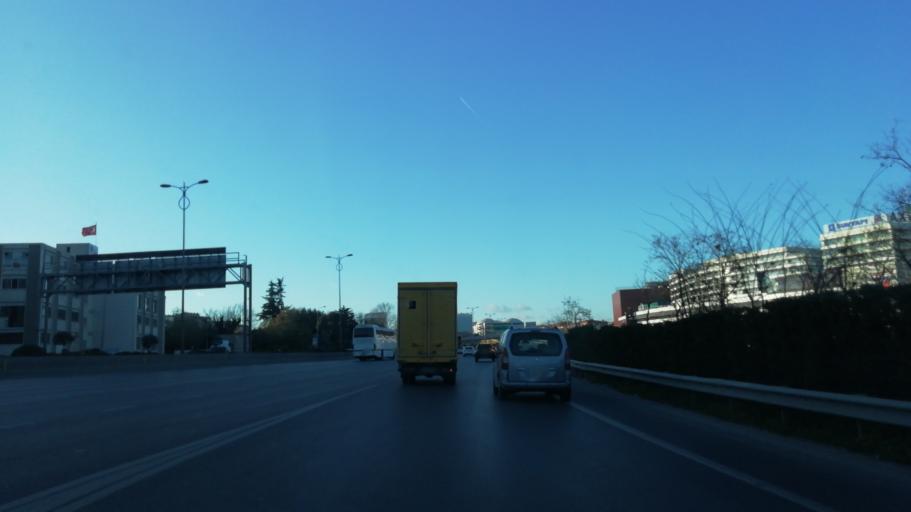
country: TR
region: Istanbul
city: Istanbul
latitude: 41.0319
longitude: 28.9210
